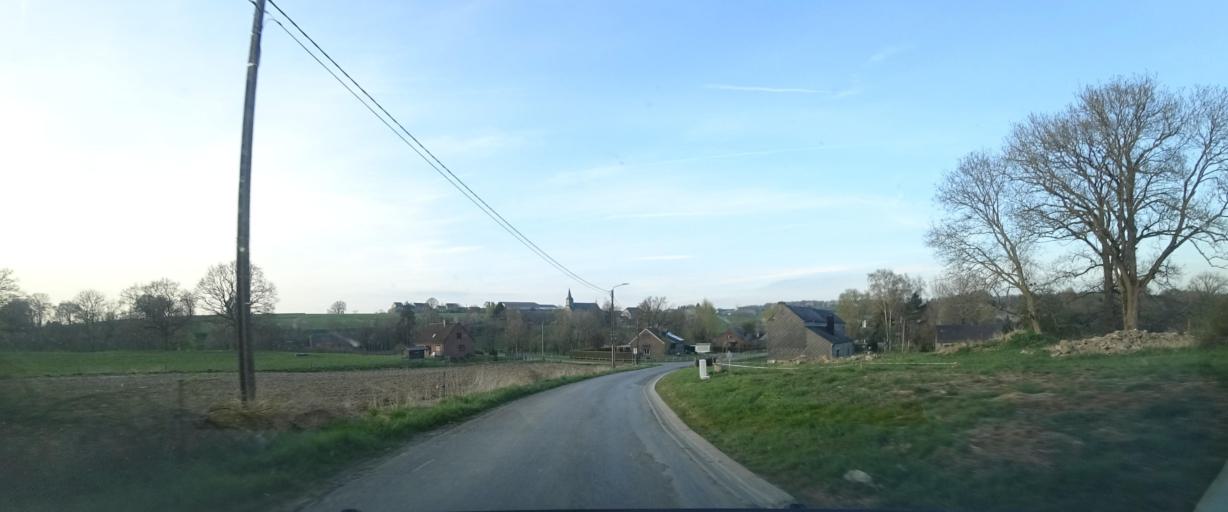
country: BE
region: Wallonia
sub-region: Province de Namur
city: Hamois
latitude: 50.3167
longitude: 5.1899
